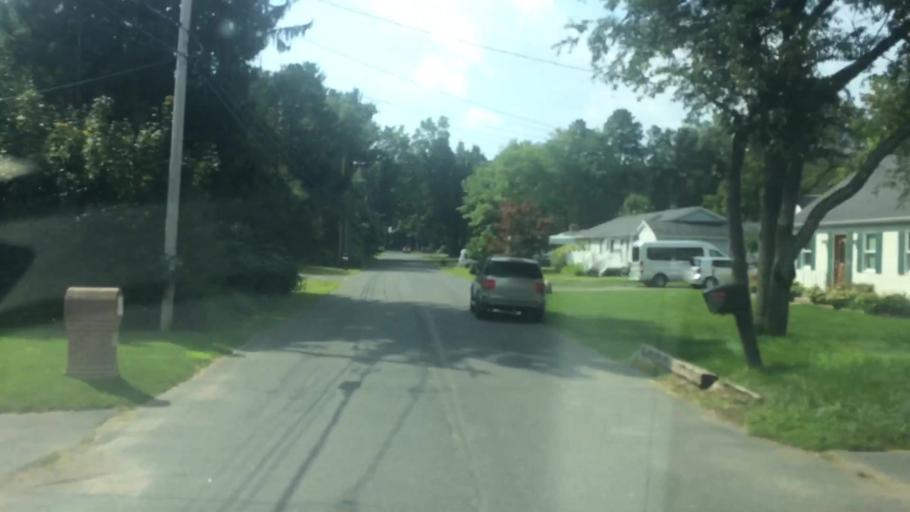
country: US
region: Massachusetts
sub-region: Hampden County
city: Westfield
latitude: 42.1400
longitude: -72.7543
